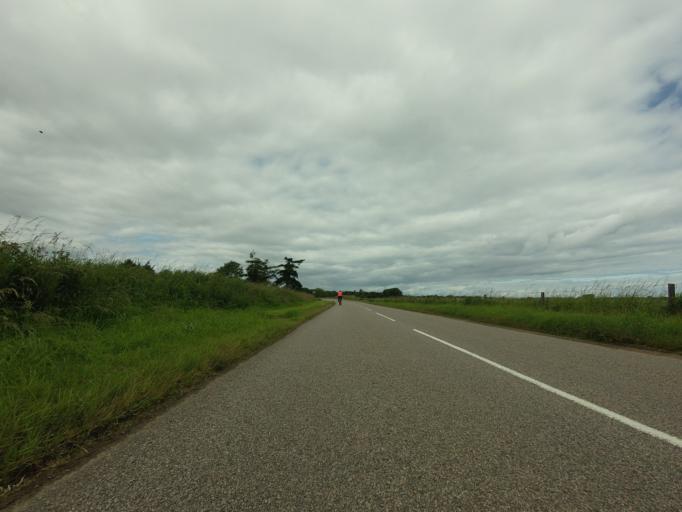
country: GB
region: Scotland
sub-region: Moray
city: Kinloss
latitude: 57.6290
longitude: -3.5503
